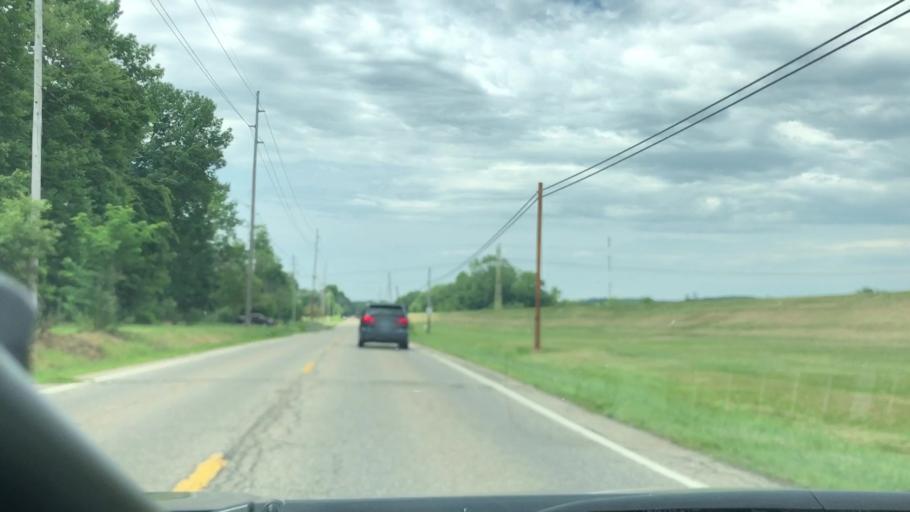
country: US
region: Ohio
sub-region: Summit County
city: New Franklin
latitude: 40.9438
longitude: -81.5342
